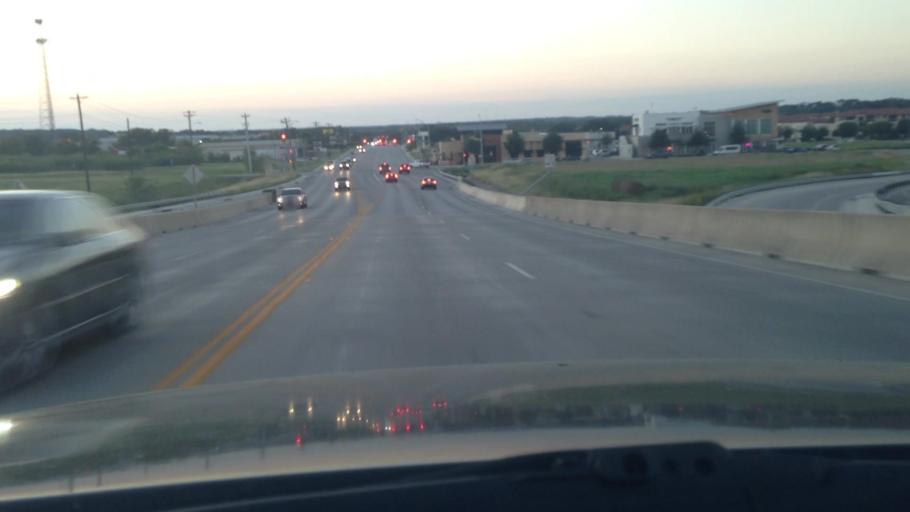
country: US
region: Texas
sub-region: Hays County
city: San Marcos
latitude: 29.8607
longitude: -97.9575
